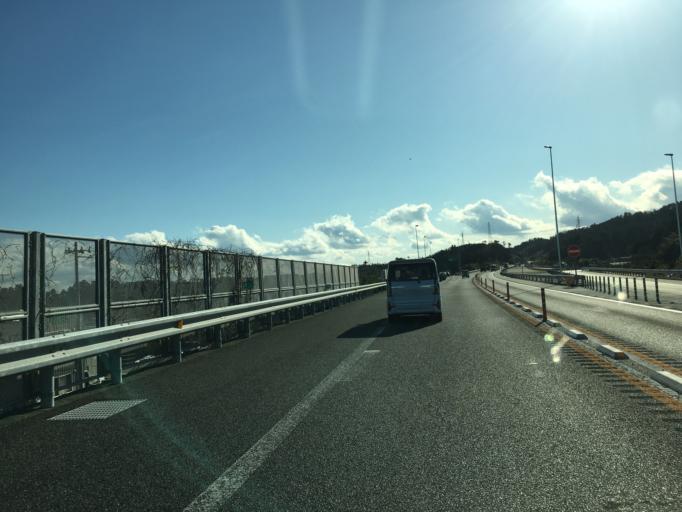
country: JP
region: Fukushima
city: Namie
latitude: 37.6614
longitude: 140.9206
